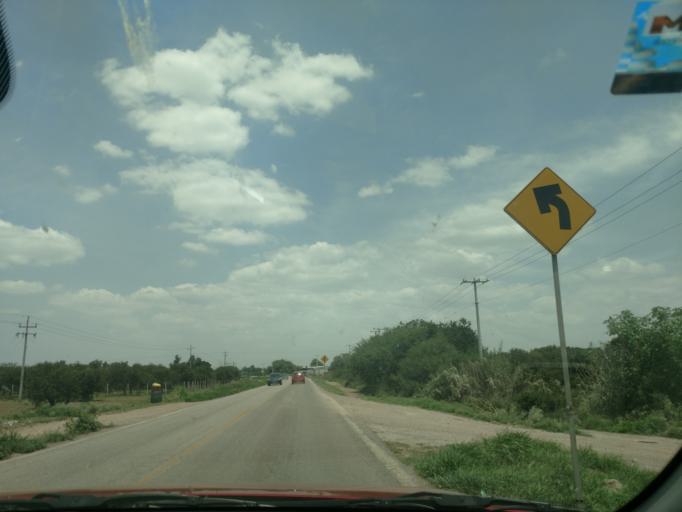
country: MX
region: San Luis Potosi
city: Ciudad Fernandez
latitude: 21.9515
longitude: -100.0653
